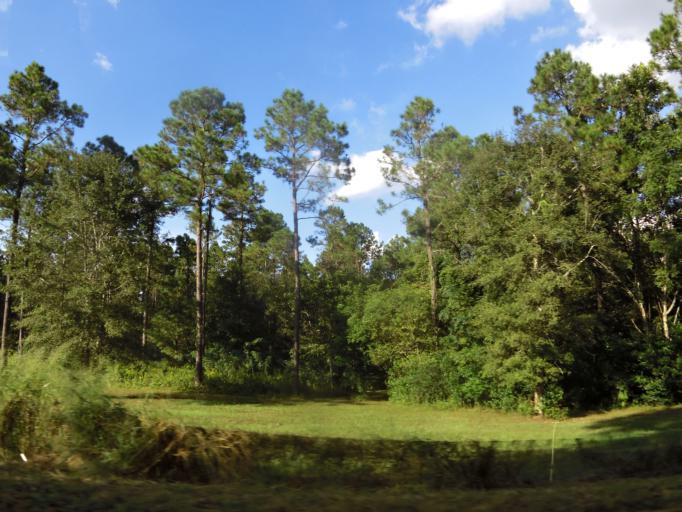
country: US
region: Georgia
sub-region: Brooks County
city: Quitman
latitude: 30.7777
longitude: -83.6128
